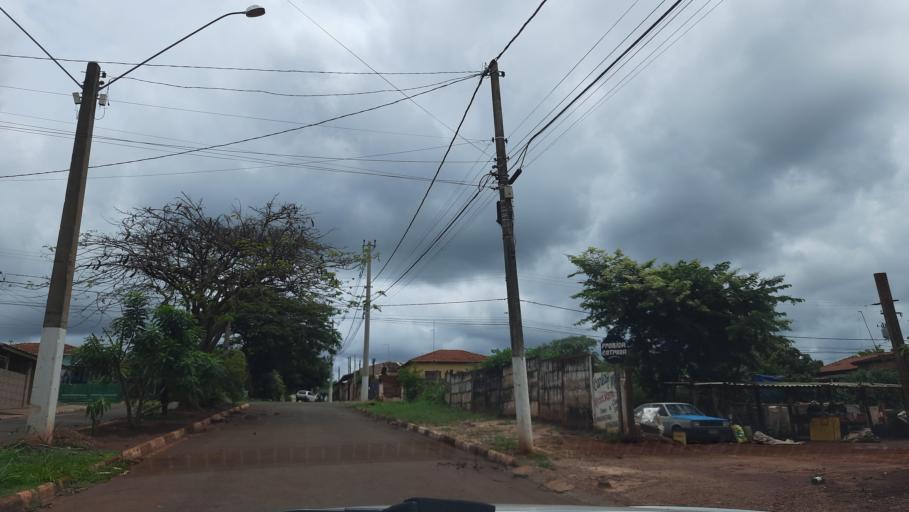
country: BR
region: Sao Paulo
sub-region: Casa Branca
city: Casa Branca
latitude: -21.7867
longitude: -47.0989
